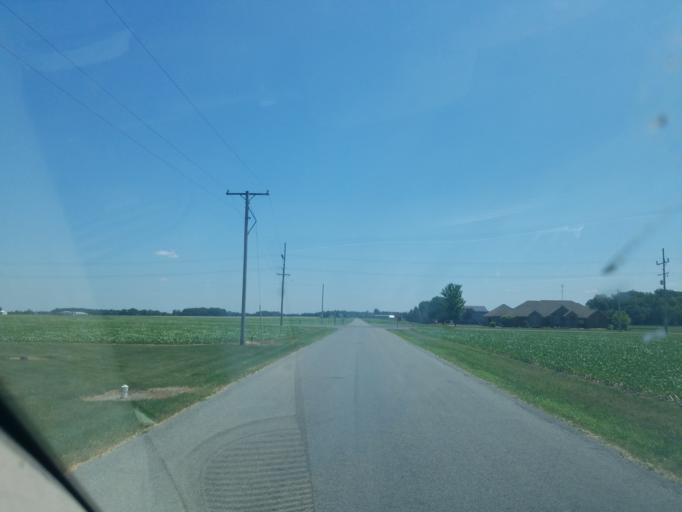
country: US
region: Ohio
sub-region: Allen County
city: Spencerville
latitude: 40.7576
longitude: -84.3600
